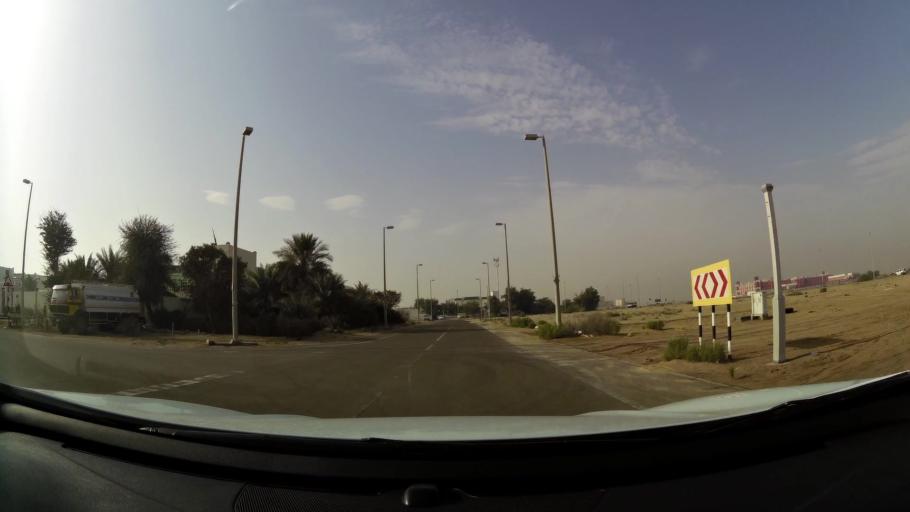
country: AE
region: Abu Dhabi
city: Abu Dhabi
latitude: 24.2662
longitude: 54.6643
